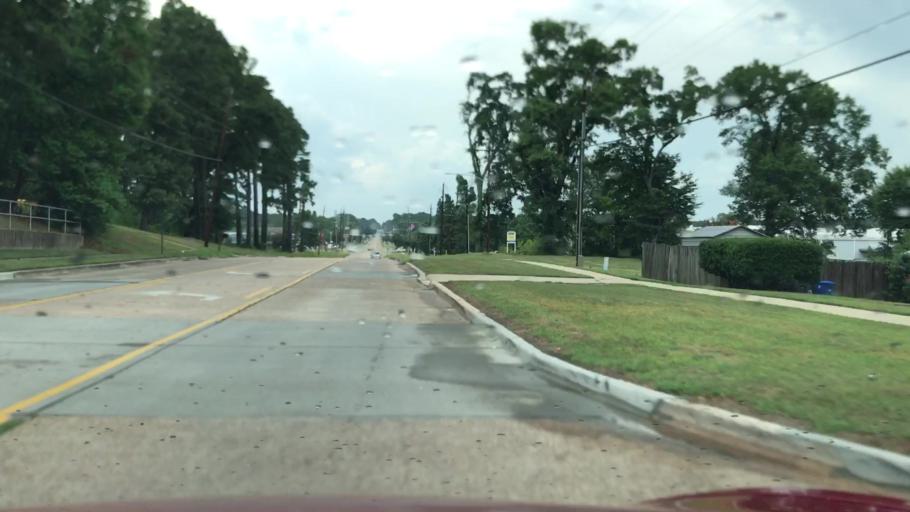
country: US
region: Louisiana
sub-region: De Soto Parish
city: Stonewall
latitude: 32.3985
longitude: -93.7804
